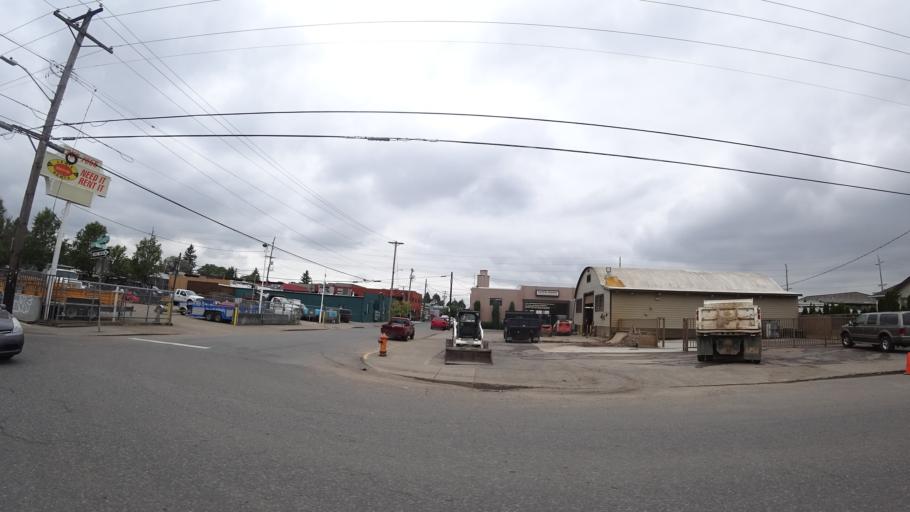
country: US
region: Oregon
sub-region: Multnomah County
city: Lents
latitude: 45.5184
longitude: -122.5814
